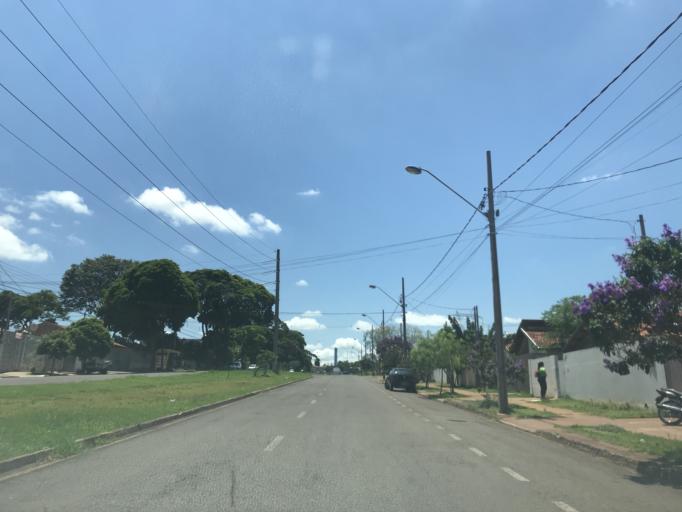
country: BR
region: Parana
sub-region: Maringa
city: Maringa
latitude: -23.4585
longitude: -51.9233
